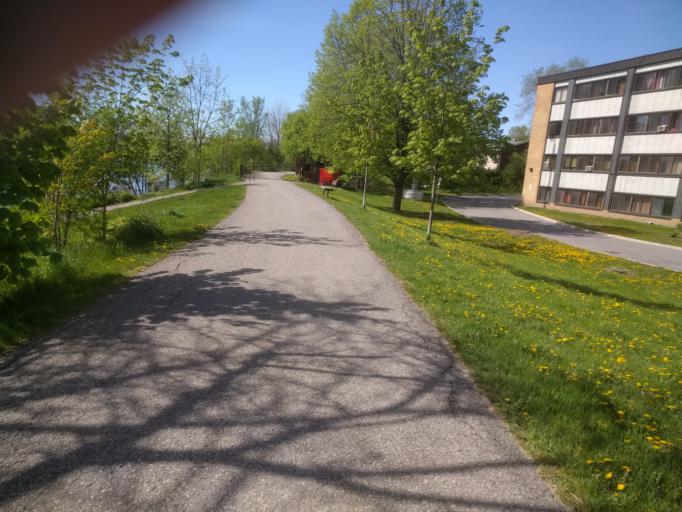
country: CA
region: Ontario
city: Ottawa
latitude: 45.3921
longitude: -75.6773
